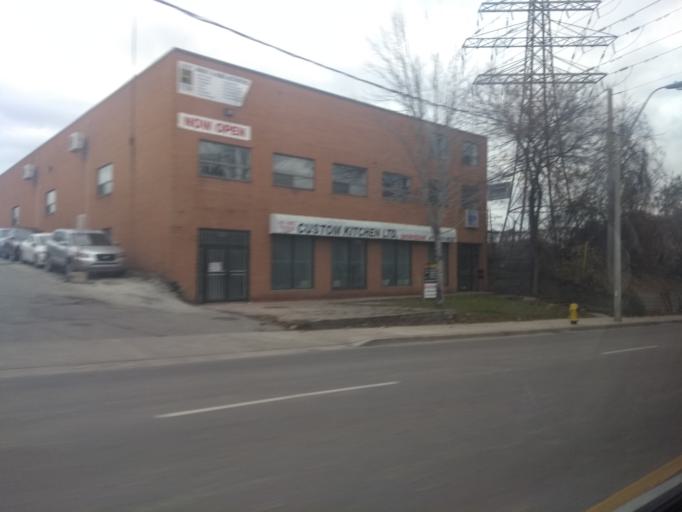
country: CA
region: Ontario
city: Toronto
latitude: 43.6767
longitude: -79.4712
